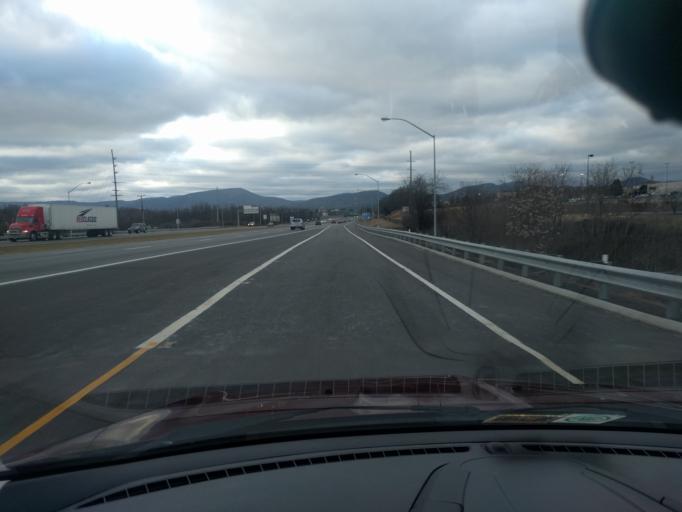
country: US
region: Virginia
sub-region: City of Roanoke
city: Roanoke
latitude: 37.2997
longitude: -79.9617
